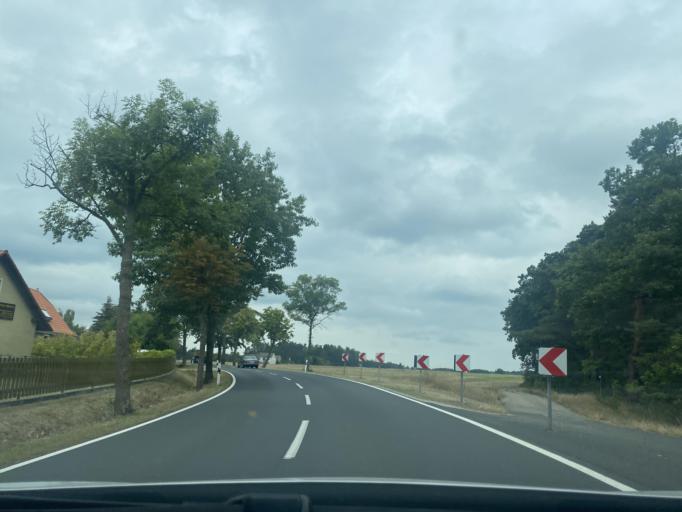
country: DE
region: Saxony
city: Mucka
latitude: 51.2814
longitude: 14.6427
